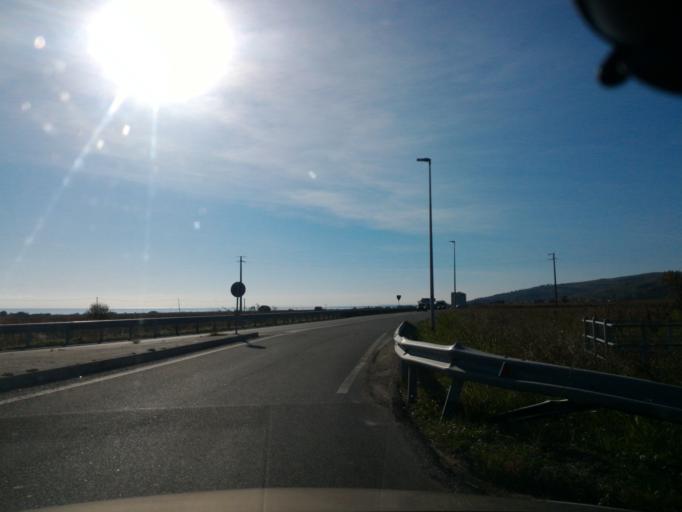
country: IT
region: Calabria
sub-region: Provincia di Crotone
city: Torre Melissa
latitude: 39.3309
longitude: 17.1086
